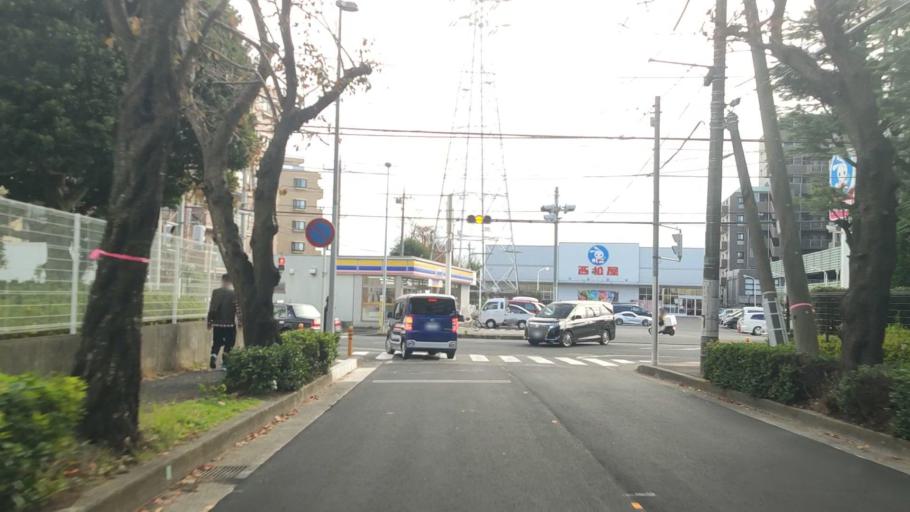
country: JP
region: Kanagawa
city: Minami-rinkan
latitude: 35.5018
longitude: 139.4521
